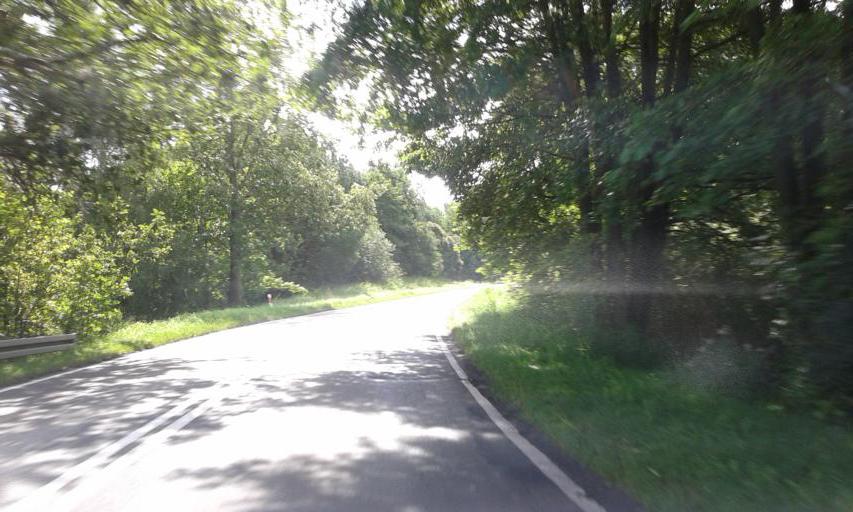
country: PL
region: West Pomeranian Voivodeship
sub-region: Powiat drawski
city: Czaplinek
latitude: 53.5451
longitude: 16.2494
